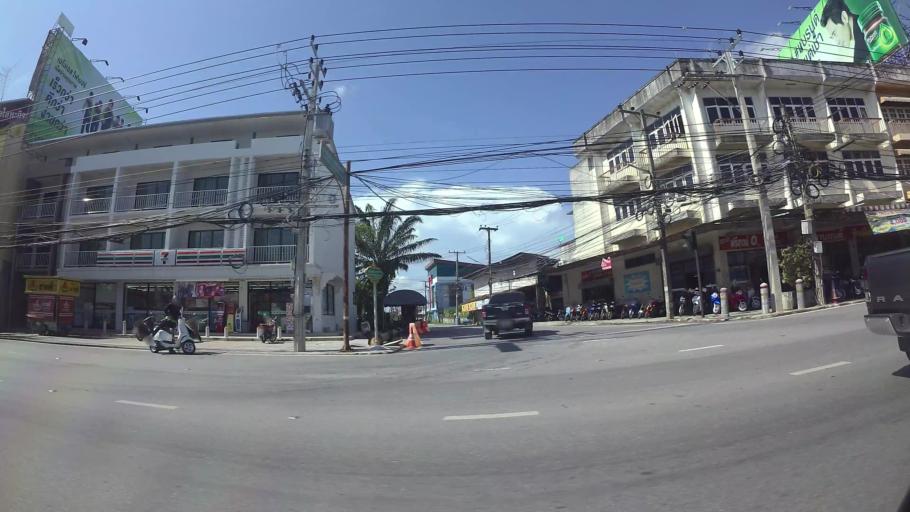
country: TH
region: Rayong
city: Rayong
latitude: 12.6810
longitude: 101.2840
